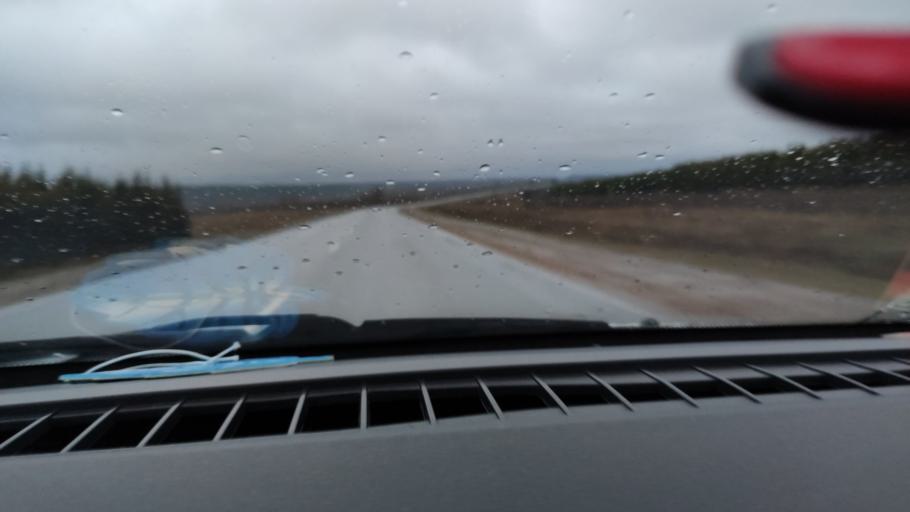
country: RU
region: Udmurtiya
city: Alnashi
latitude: 56.1649
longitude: 52.4798
